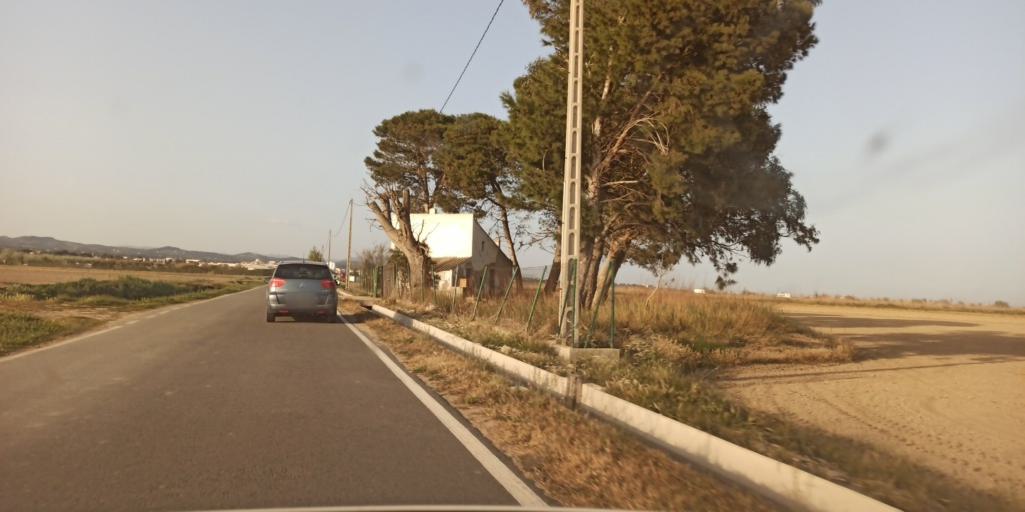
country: ES
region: Catalonia
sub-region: Provincia de Tarragona
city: L'Ampolla
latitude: 40.7926
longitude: 0.6985
